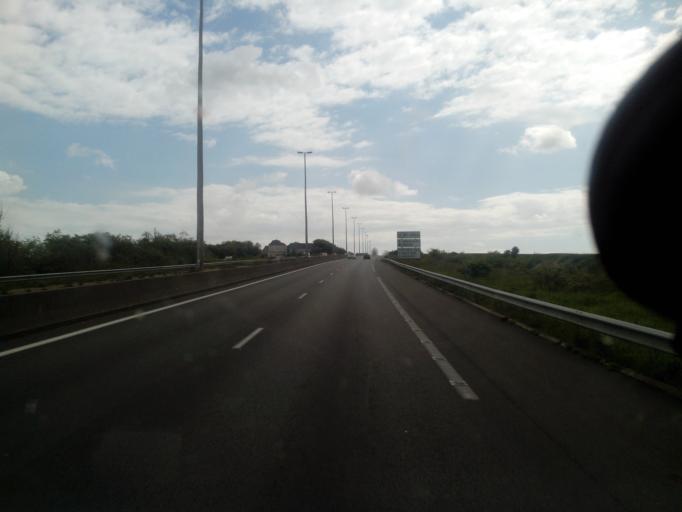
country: FR
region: Nord-Pas-de-Calais
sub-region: Departement du Pas-de-Calais
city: Ferques
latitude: 50.8873
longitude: 1.7558
